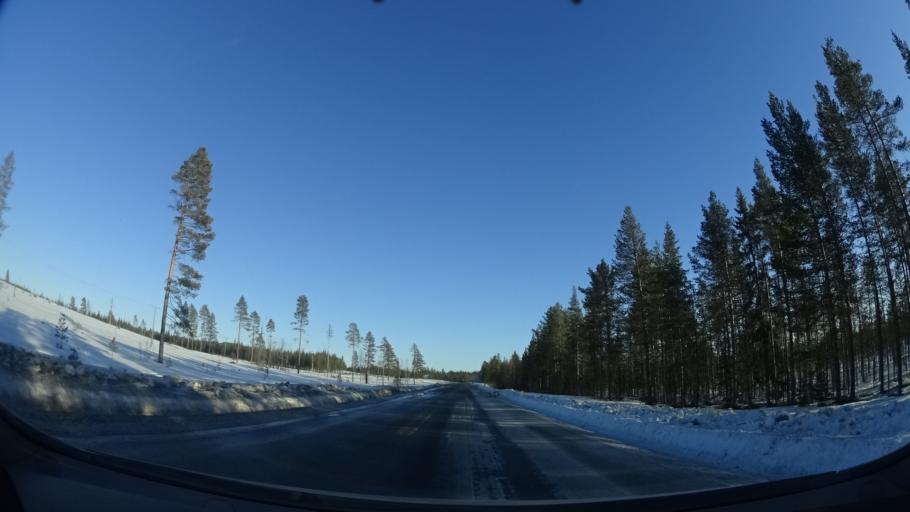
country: SE
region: Vaesterbotten
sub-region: Skelleftea Kommun
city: Langsele
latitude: 65.0359
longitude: 20.0952
